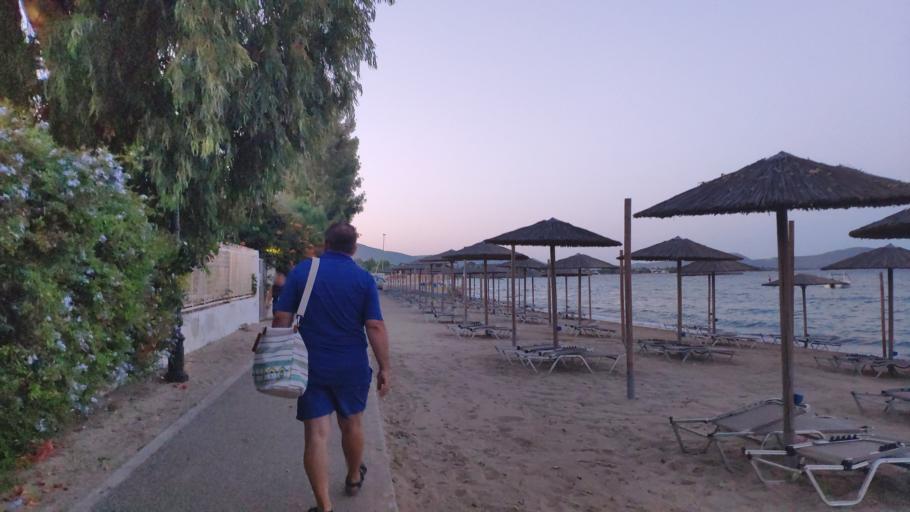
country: GR
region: Attica
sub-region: Nomarchia Anatolikis Attikis
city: Aghios Panteleimon
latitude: 38.1040
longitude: 23.9804
